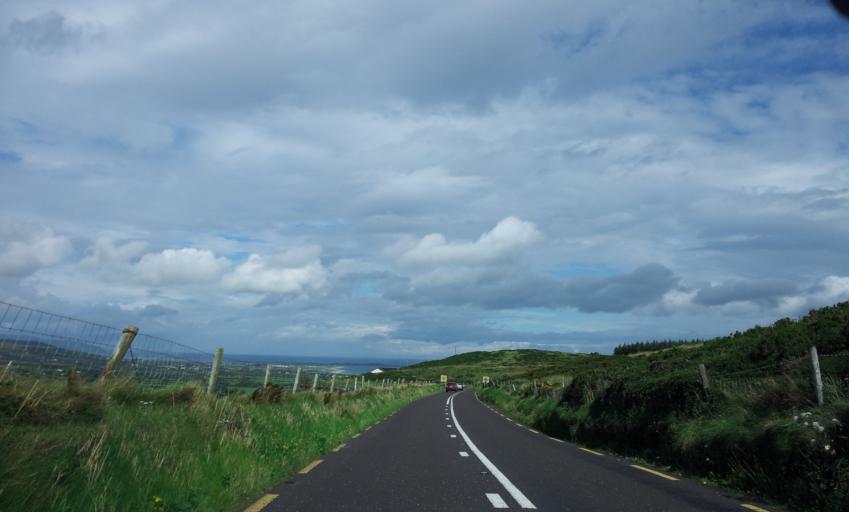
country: IE
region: Munster
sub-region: Ciarrai
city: Killorglin
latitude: 52.2116
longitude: -9.9362
